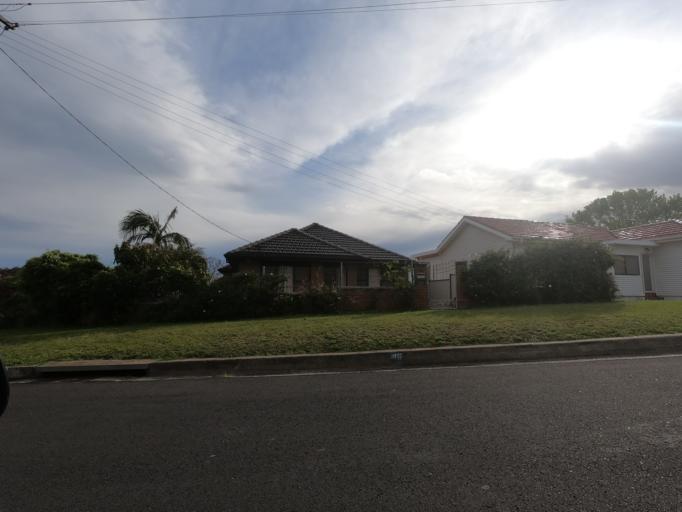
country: AU
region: New South Wales
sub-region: Wollongong
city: Lake Heights
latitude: -34.4874
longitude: 150.8689
